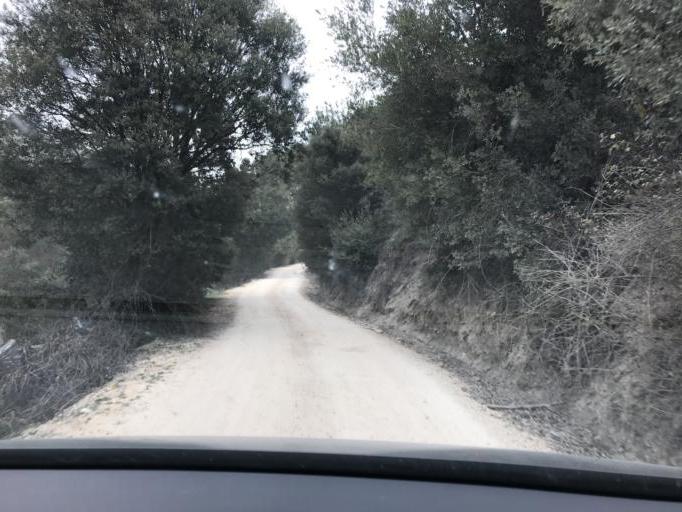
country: ES
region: Andalusia
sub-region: Provincia de Granada
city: Castril
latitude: 37.8763
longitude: -2.7571
